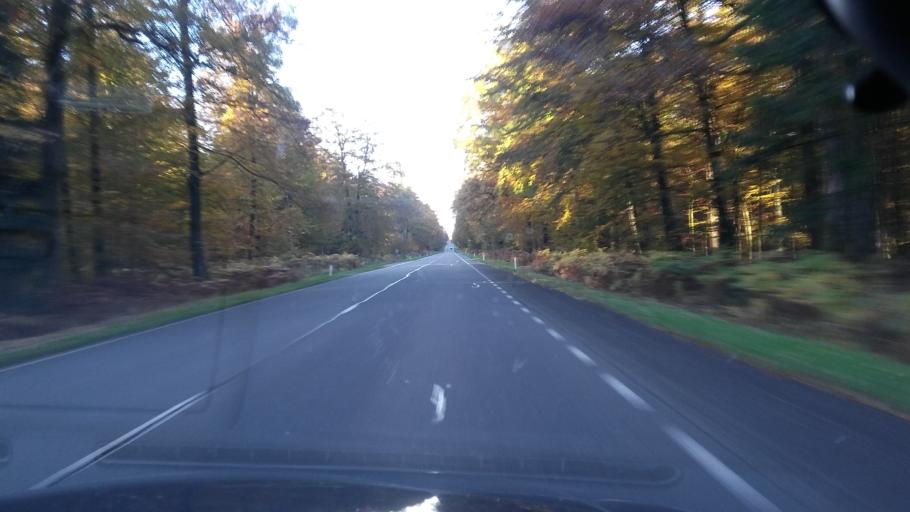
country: BE
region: Wallonia
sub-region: Province du Luxembourg
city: Herbeumont
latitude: 49.7398
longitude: 5.2222
